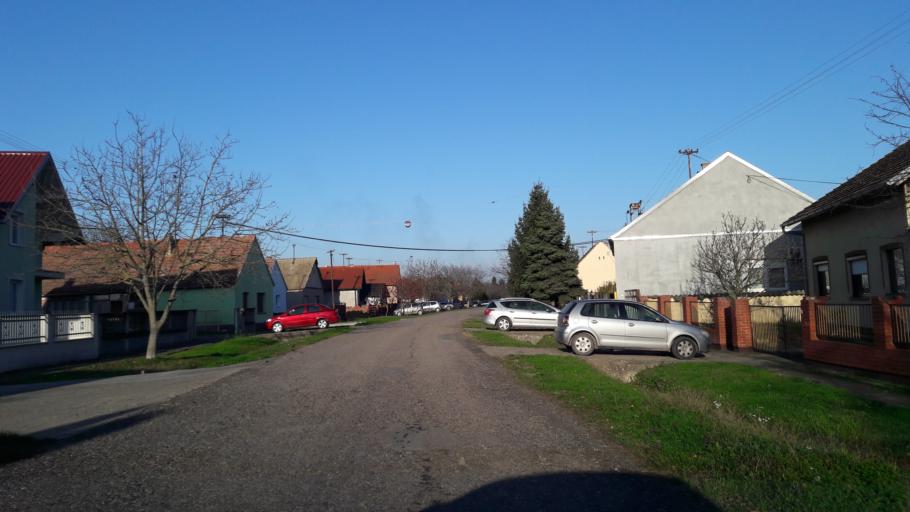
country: HR
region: Osjecko-Baranjska
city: Viskovci
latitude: 45.3372
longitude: 18.4495
